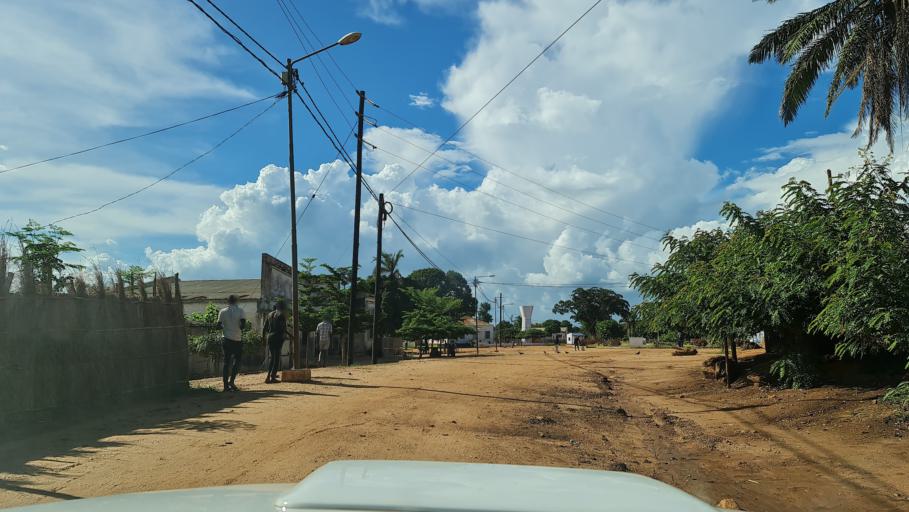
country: MZ
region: Nampula
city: Ilha de Mocambique
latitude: -15.2897
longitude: 40.1151
